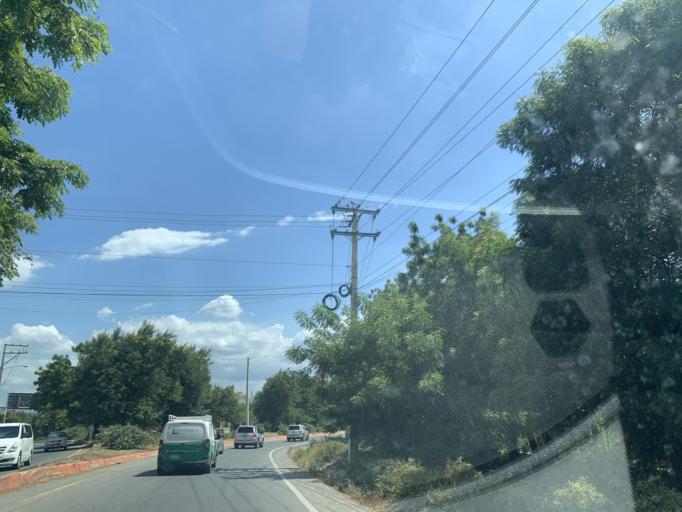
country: DO
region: Santiago
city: Villa Bisono
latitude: 19.5567
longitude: -70.8601
